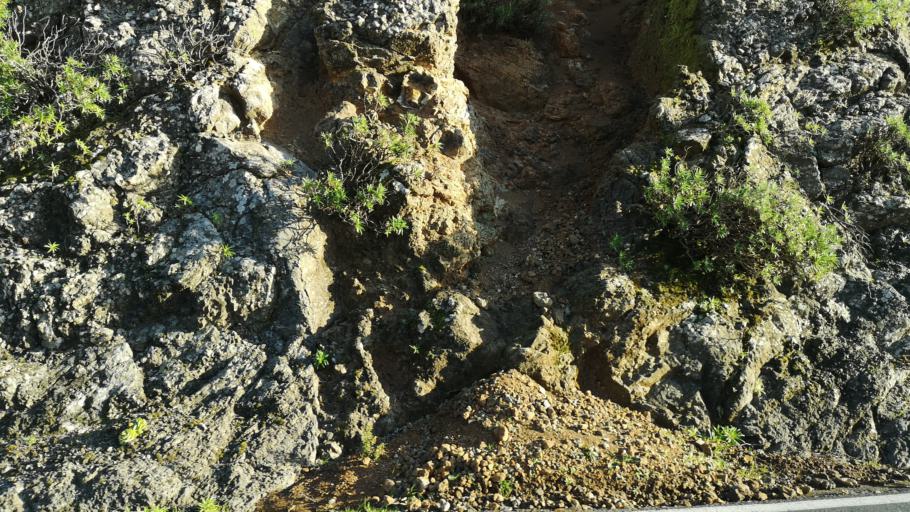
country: ES
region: Canary Islands
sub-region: Provincia de Santa Cruz de Tenerife
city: Alajero
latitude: 28.0932
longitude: -17.2487
